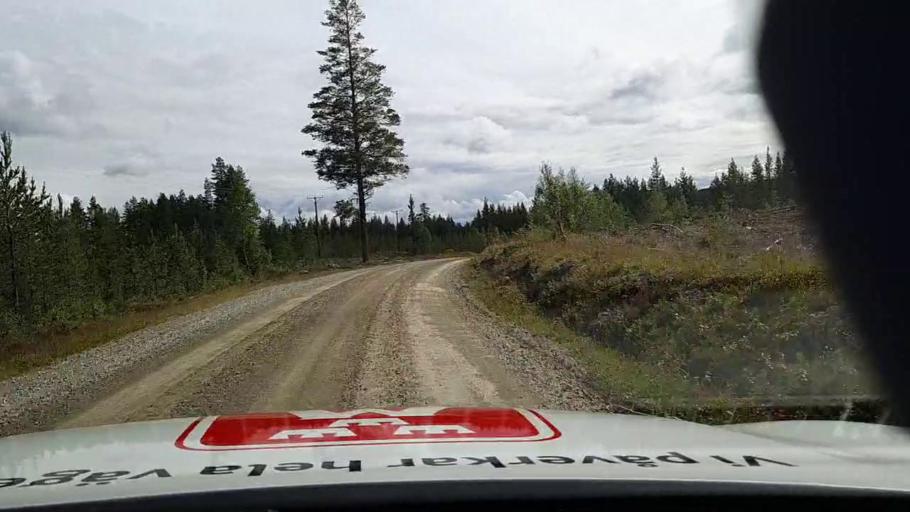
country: SE
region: Jaemtland
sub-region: Are Kommun
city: Jarpen
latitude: 62.5026
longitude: 13.5015
